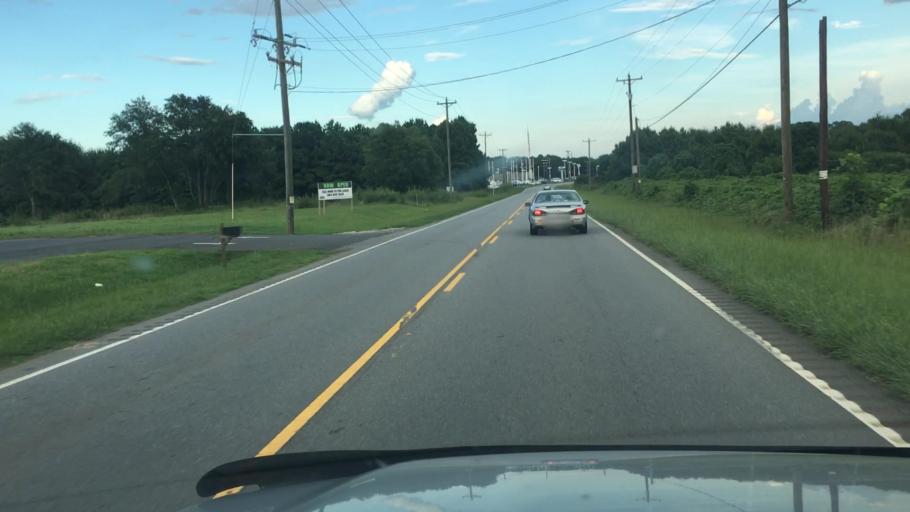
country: US
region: South Carolina
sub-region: Cherokee County
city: Gaffney
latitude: 35.1040
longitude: -81.6867
